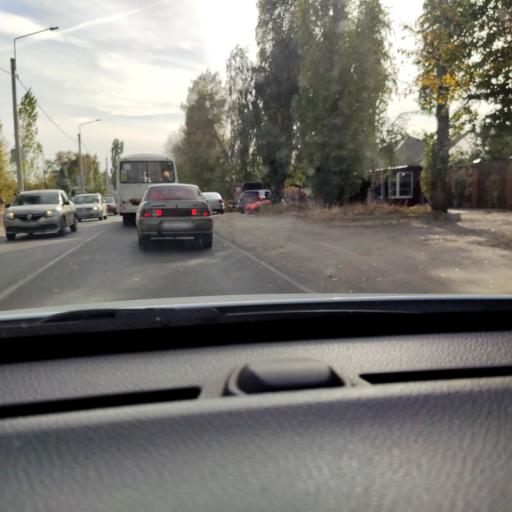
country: RU
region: Voronezj
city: Maslovka
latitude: 51.5517
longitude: 39.2355
